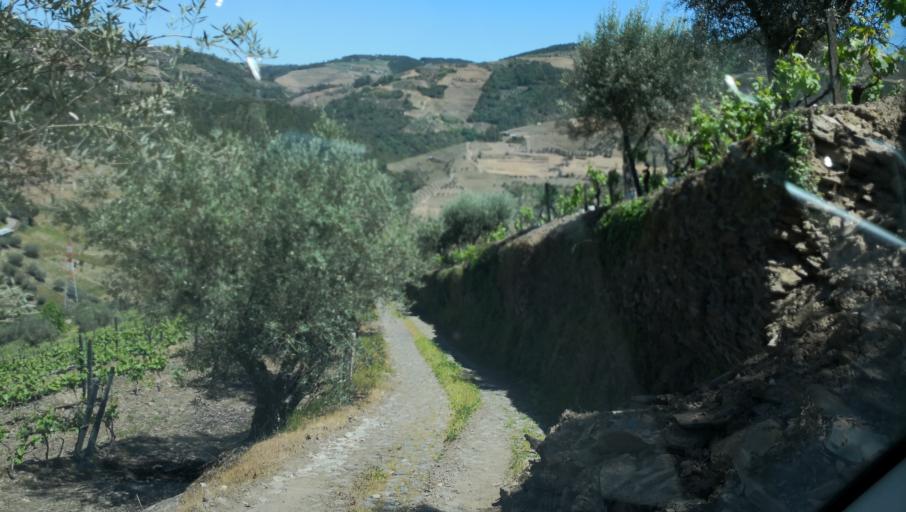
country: PT
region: Vila Real
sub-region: Santa Marta de Penaguiao
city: Santa Marta de Penaguiao
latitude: 41.2254
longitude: -7.7249
